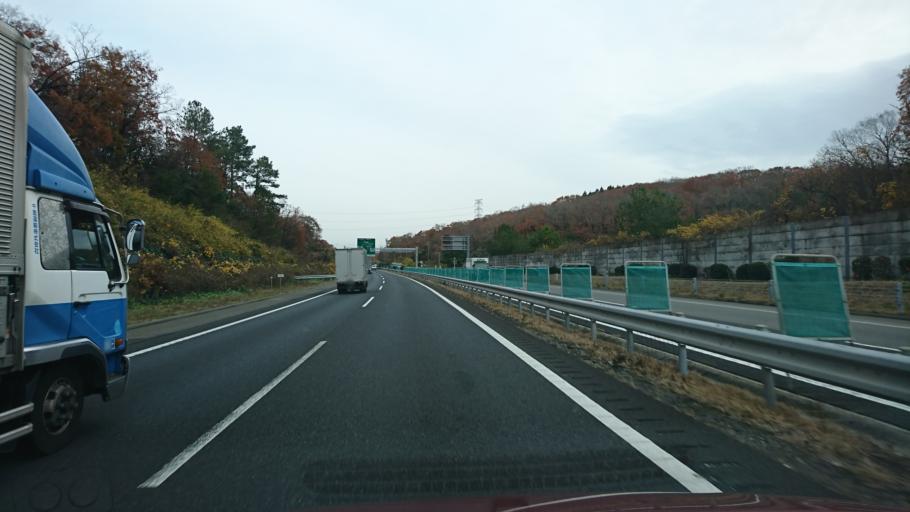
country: JP
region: Hyogo
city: Sandacho
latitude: 34.8299
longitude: 135.1845
